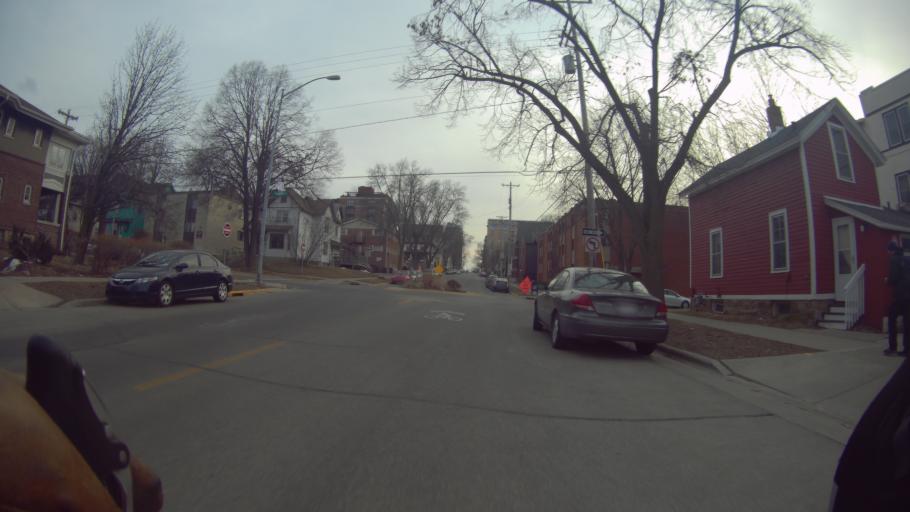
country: US
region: Wisconsin
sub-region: Dane County
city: Madison
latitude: 43.0789
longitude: -89.3803
